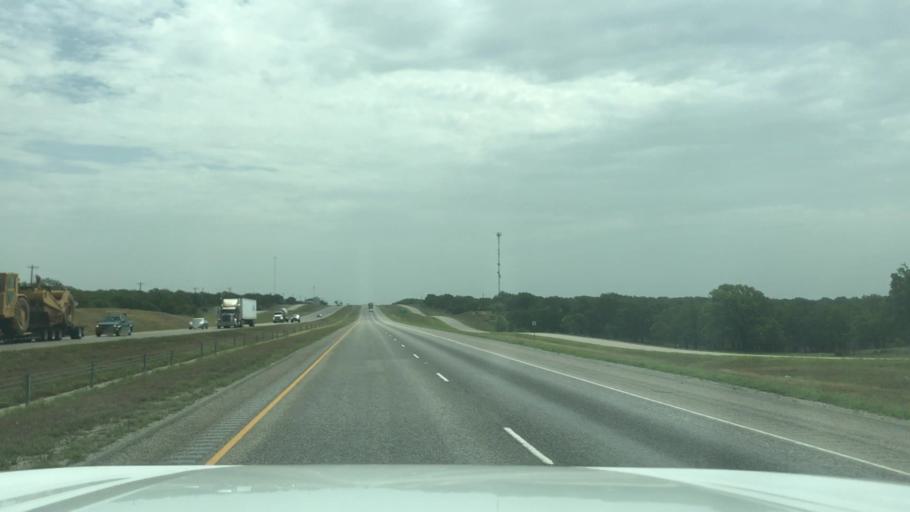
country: US
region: Texas
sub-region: Eastland County
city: Cisco
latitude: 32.3753
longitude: -98.9560
